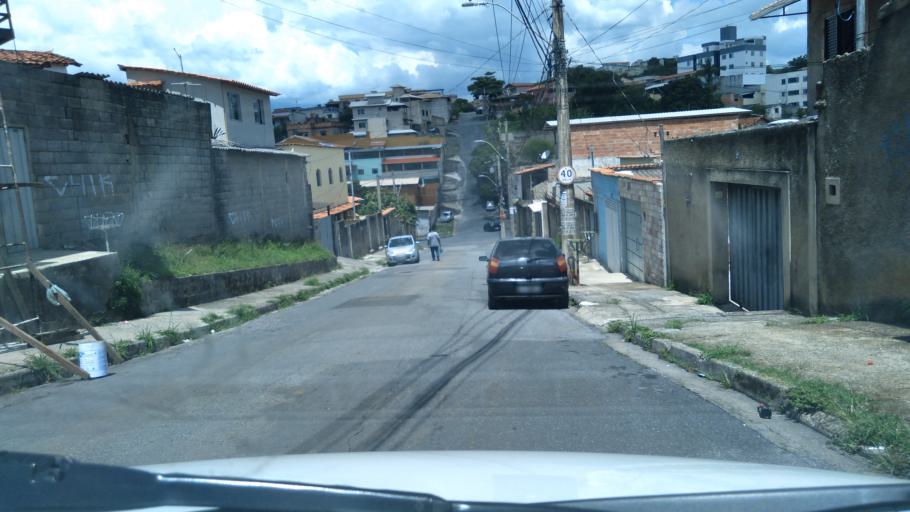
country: BR
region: Minas Gerais
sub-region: Belo Horizonte
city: Belo Horizonte
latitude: -19.8630
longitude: -43.8990
